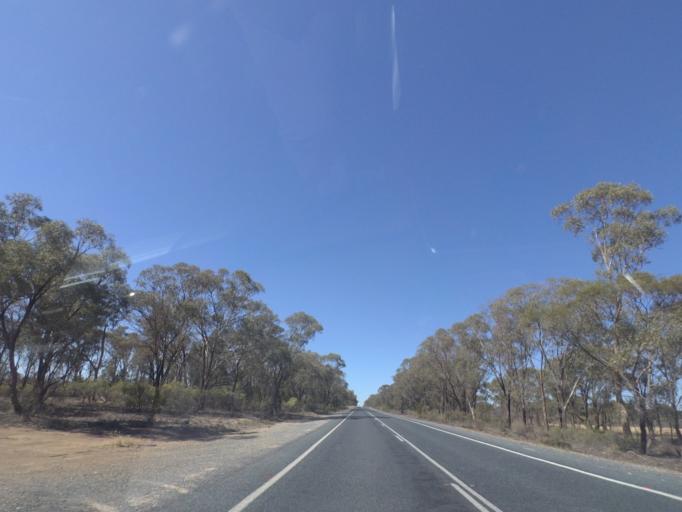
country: AU
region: New South Wales
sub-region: Bland
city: West Wyalong
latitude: -34.1212
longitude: 147.1272
